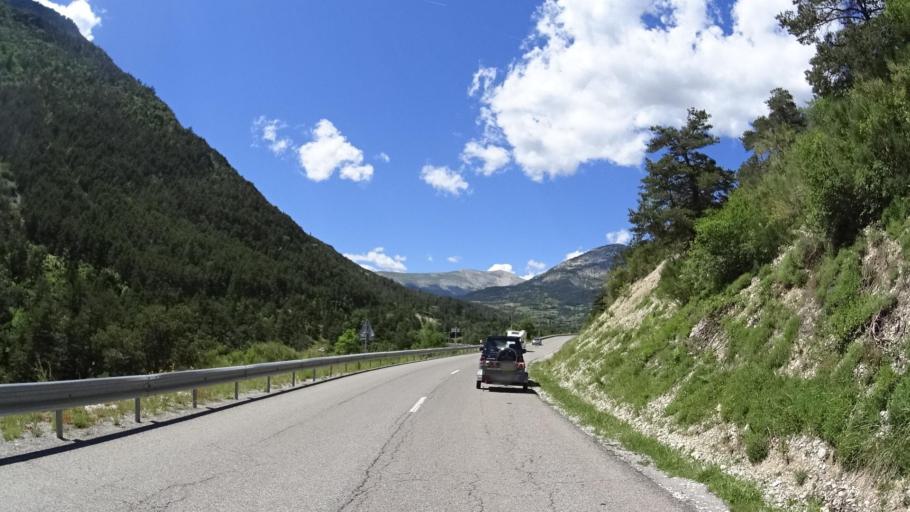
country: FR
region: Provence-Alpes-Cote d'Azur
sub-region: Departement des Alpes-de-Haute-Provence
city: Annot
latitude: 44.0748
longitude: 6.5716
